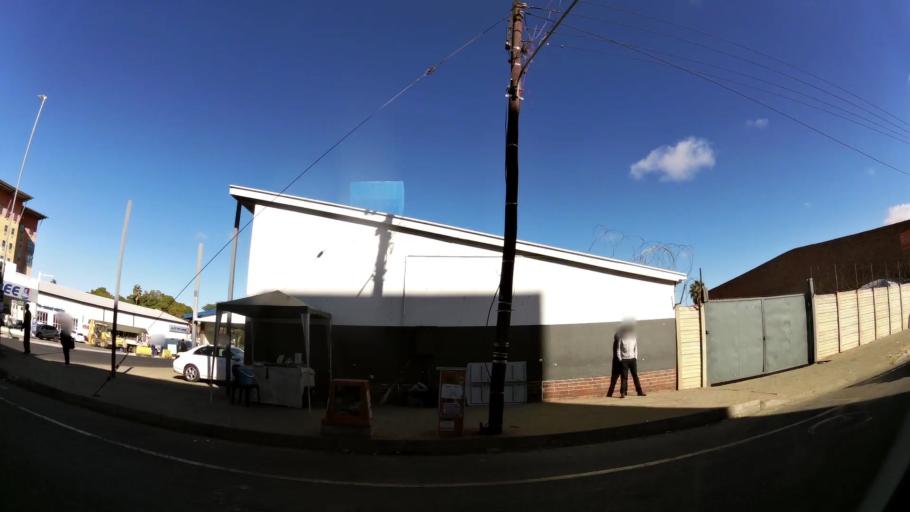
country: ZA
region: Limpopo
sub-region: Capricorn District Municipality
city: Polokwane
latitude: -23.9117
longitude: 29.4502
